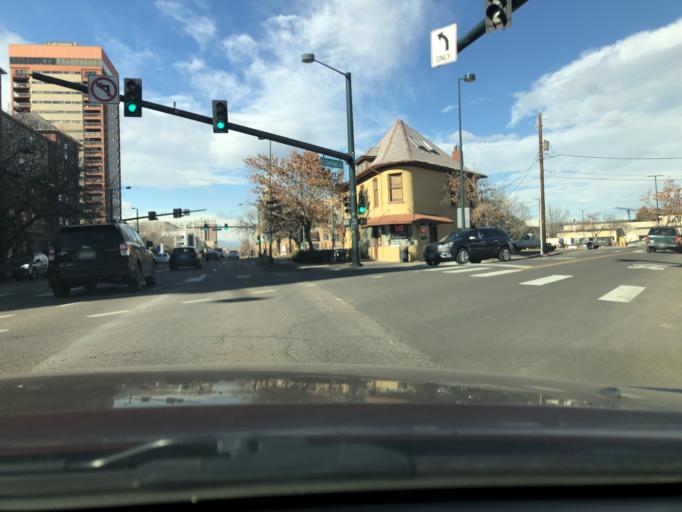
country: US
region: Colorado
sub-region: Denver County
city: Denver
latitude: 39.7470
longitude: -104.9774
